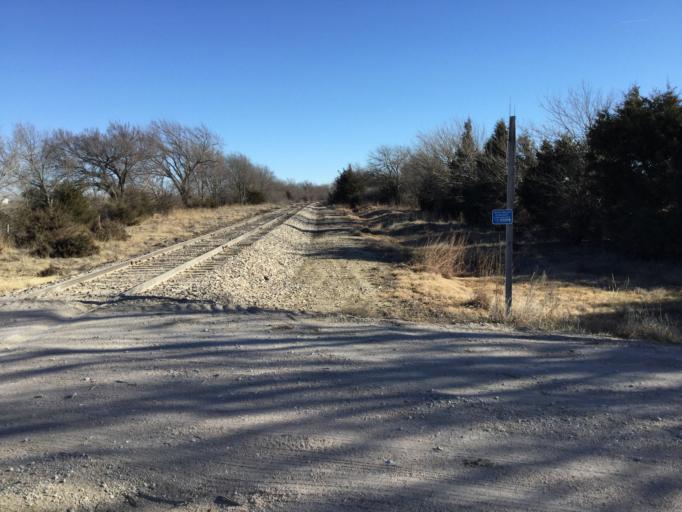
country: US
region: Kansas
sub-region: Butler County
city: Andover
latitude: 37.7920
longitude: -97.0989
